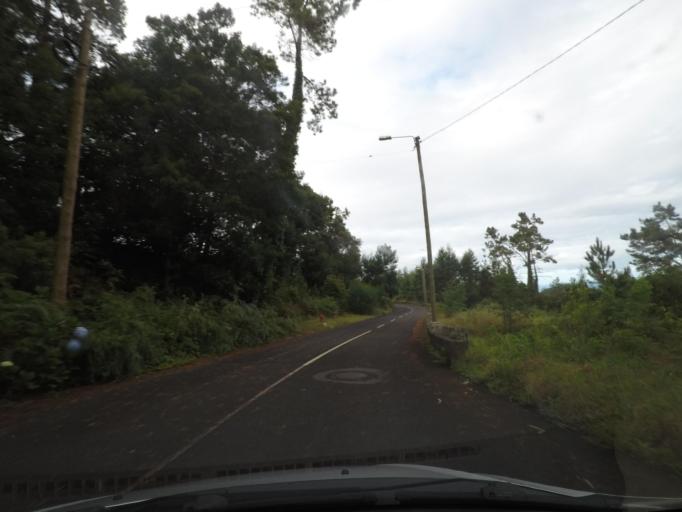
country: PT
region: Madeira
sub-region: Santana
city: Santana
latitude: 32.7889
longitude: -16.8796
